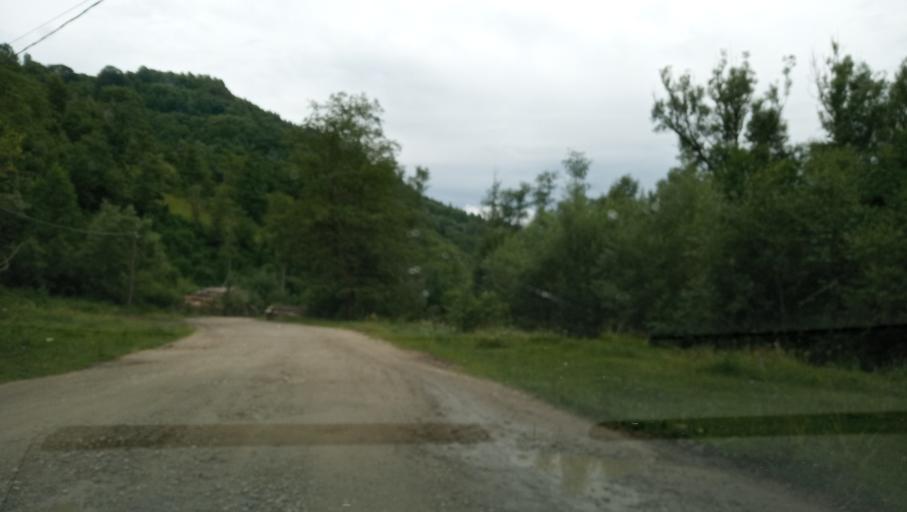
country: RO
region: Hunedoara
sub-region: Oras Petrila
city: Petrila
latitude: 45.4695
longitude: 23.4187
